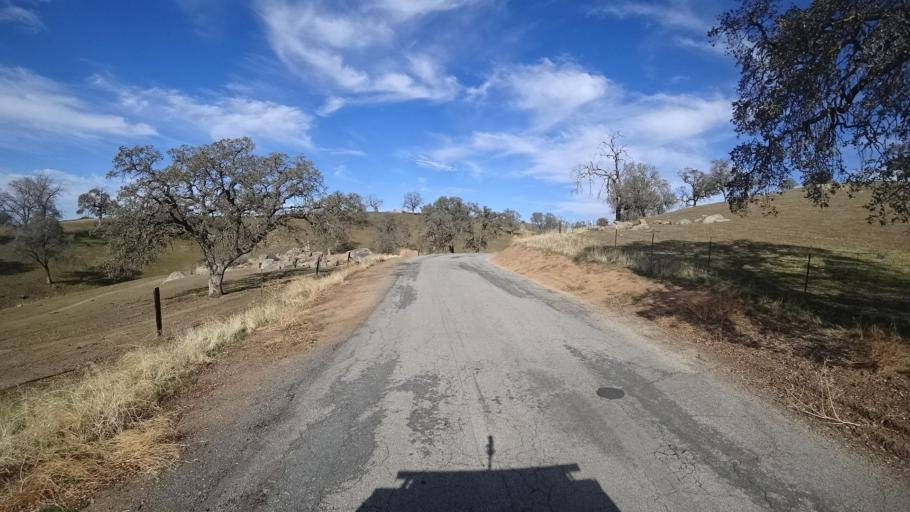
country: US
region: California
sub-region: Kern County
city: Oildale
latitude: 35.6155
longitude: -118.8480
